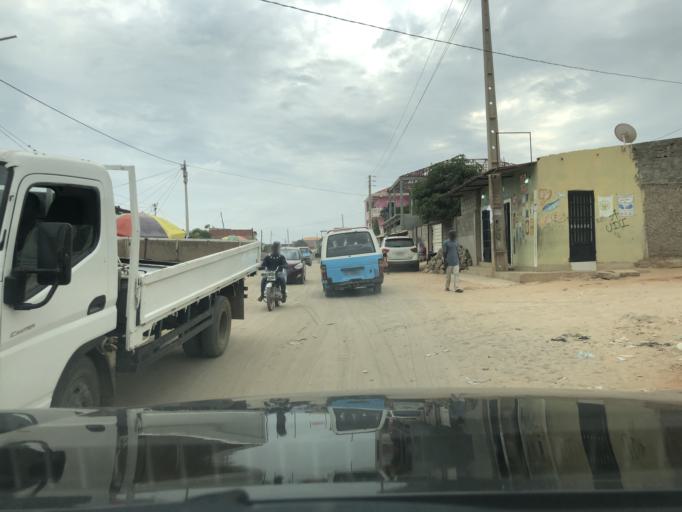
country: AO
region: Luanda
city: Luanda
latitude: -8.9334
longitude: 13.2320
